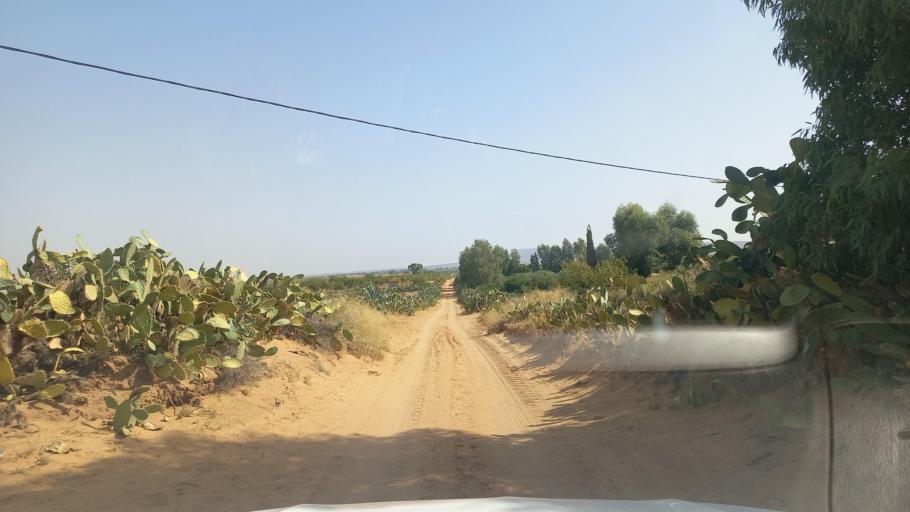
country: TN
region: Al Qasrayn
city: Kasserine
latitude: 35.2320
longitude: 9.0519
